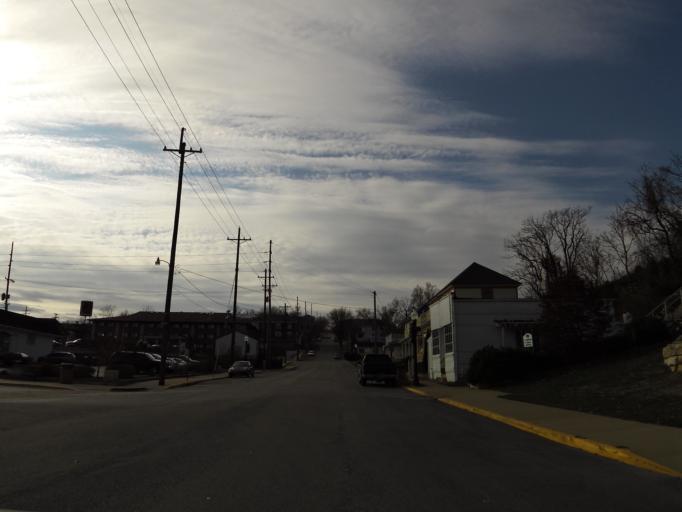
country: US
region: Missouri
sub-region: Marion County
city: Hannibal
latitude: 39.7129
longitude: -91.3578
